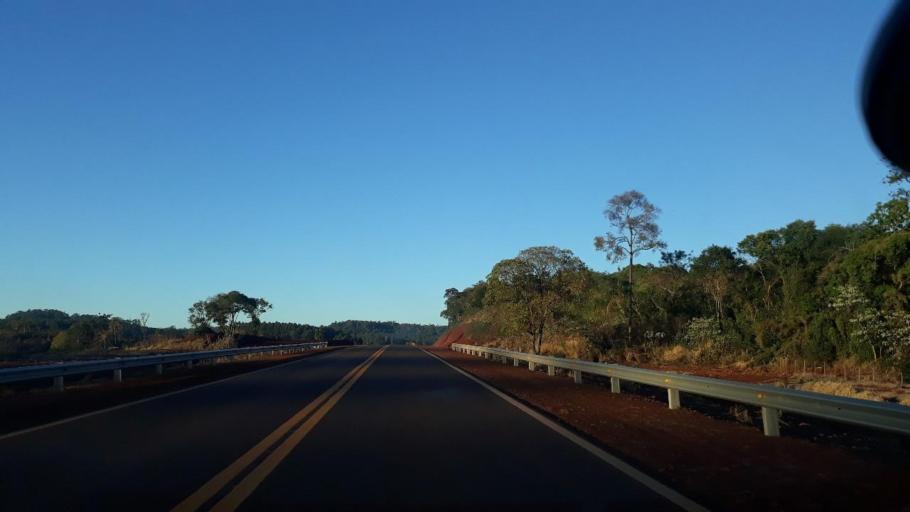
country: AR
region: Misiones
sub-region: Departamento de San Pedro
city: San Pedro
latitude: -26.5433
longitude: -53.9599
